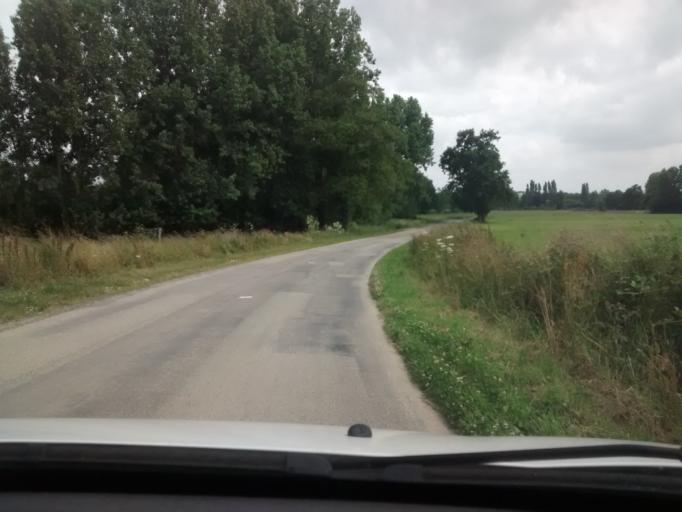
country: FR
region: Brittany
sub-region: Departement d'Ille-et-Vilaine
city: Acigne
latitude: 48.1240
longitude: -1.5392
